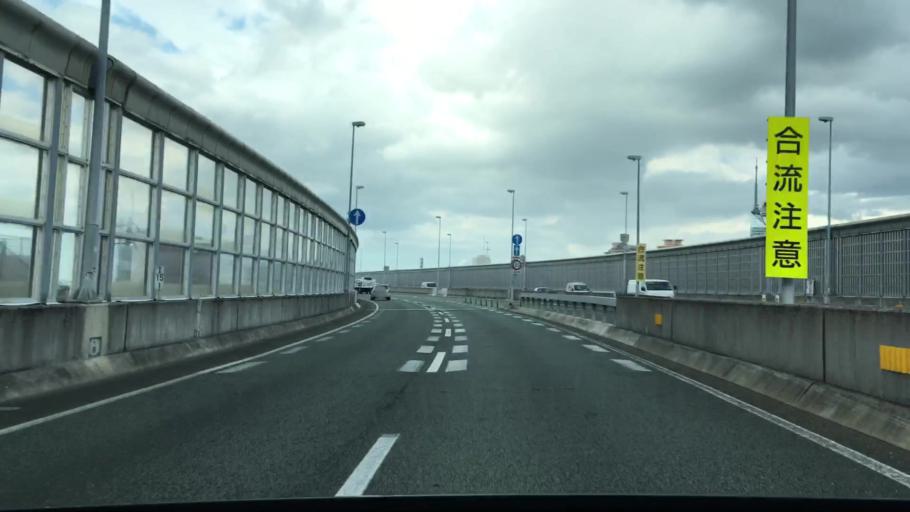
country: JP
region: Fukuoka
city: Fukuoka-shi
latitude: 33.5844
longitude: 130.3401
